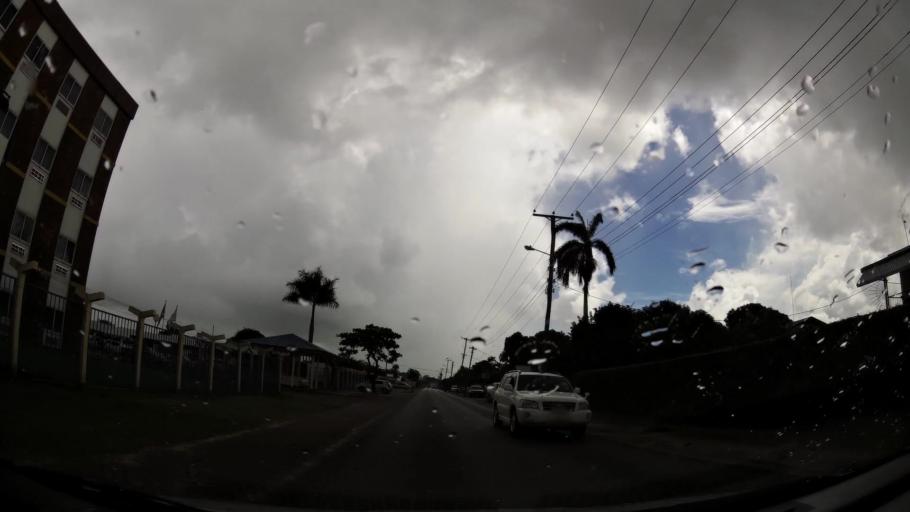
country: SR
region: Paramaribo
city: Paramaribo
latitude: 5.8385
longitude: -55.2013
